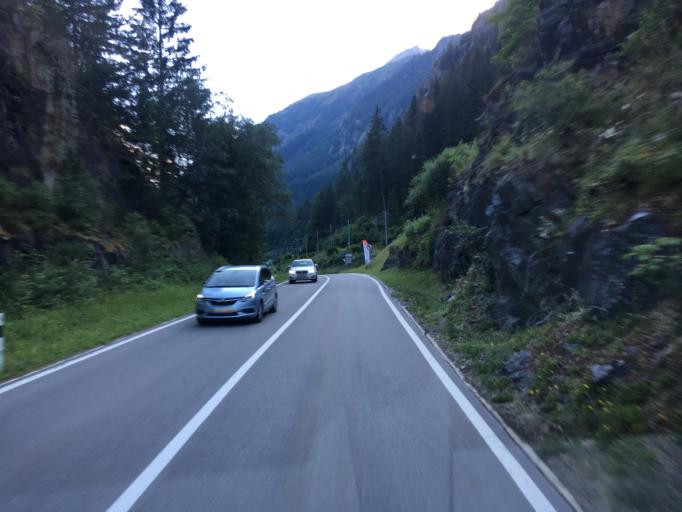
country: CH
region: Valais
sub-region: Saint-Maurice District
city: Salvan
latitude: 46.0561
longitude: 6.9556
